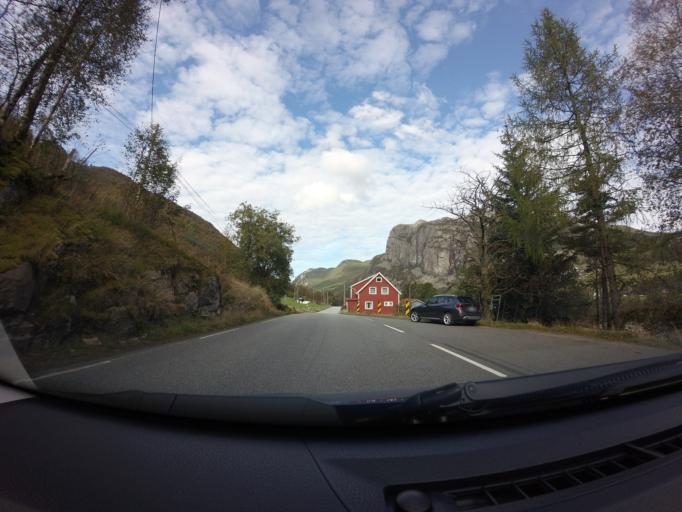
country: NO
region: Rogaland
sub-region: Forsand
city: Forsand
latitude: 58.7998
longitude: 6.2665
